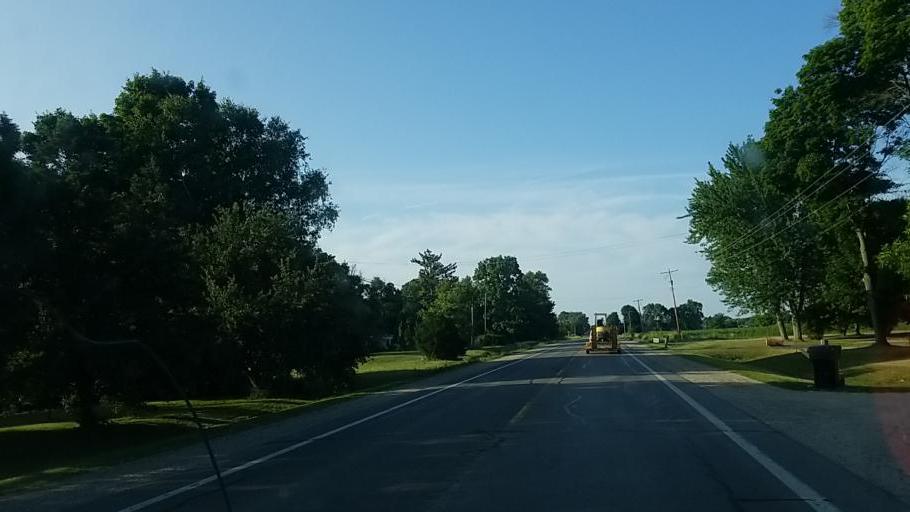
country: US
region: Michigan
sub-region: Montcalm County
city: Stanton
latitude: 43.2026
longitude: -85.0737
